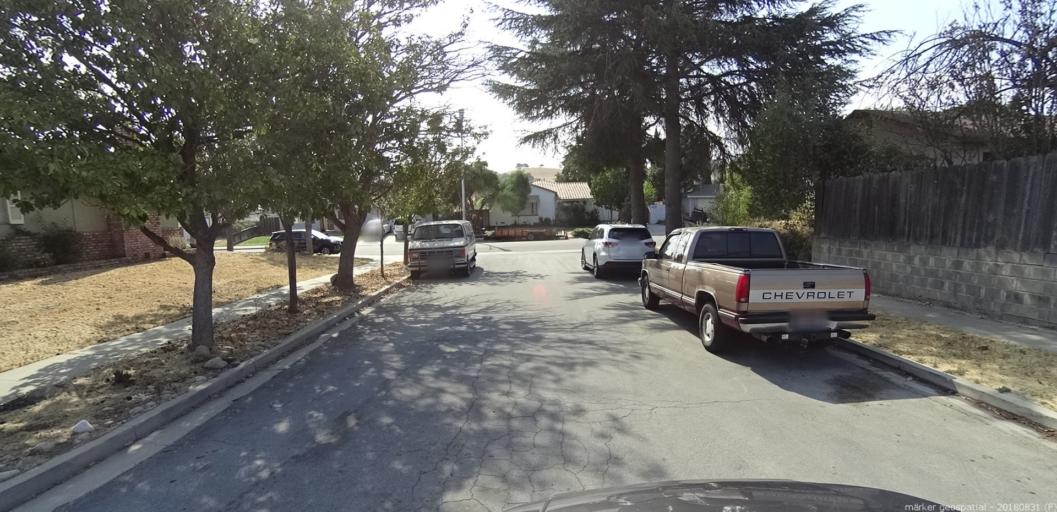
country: US
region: California
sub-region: Monterey County
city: King City
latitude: 36.1839
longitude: -121.1472
